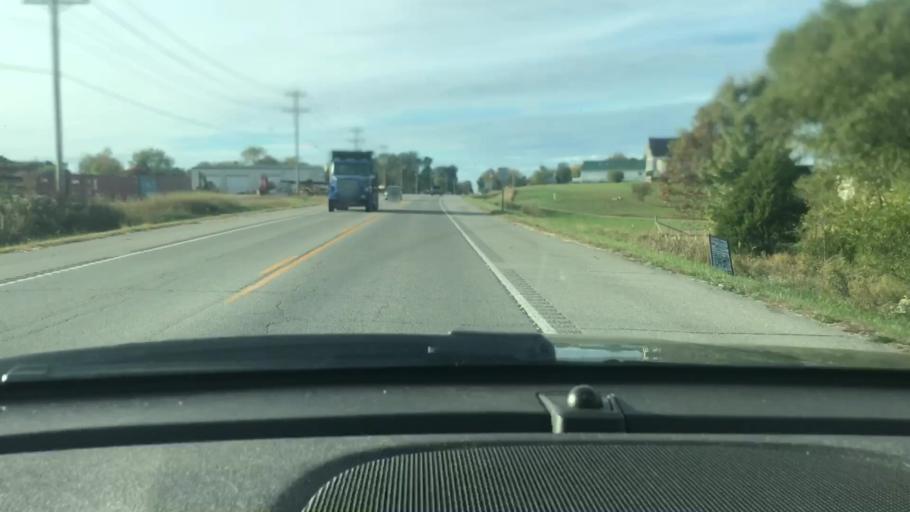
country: US
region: Tennessee
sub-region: Dickson County
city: White Bluff
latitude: 36.1326
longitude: -87.2343
